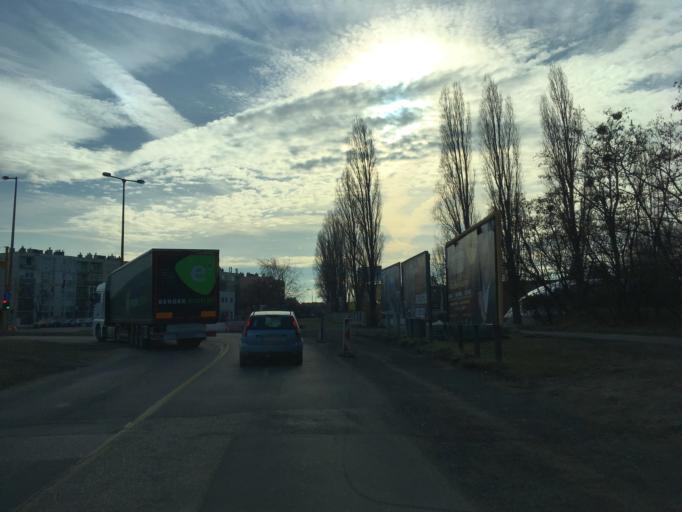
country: HU
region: Gyor-Moson-Sopron
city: Gyor
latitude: 47.6963
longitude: 17.6600
